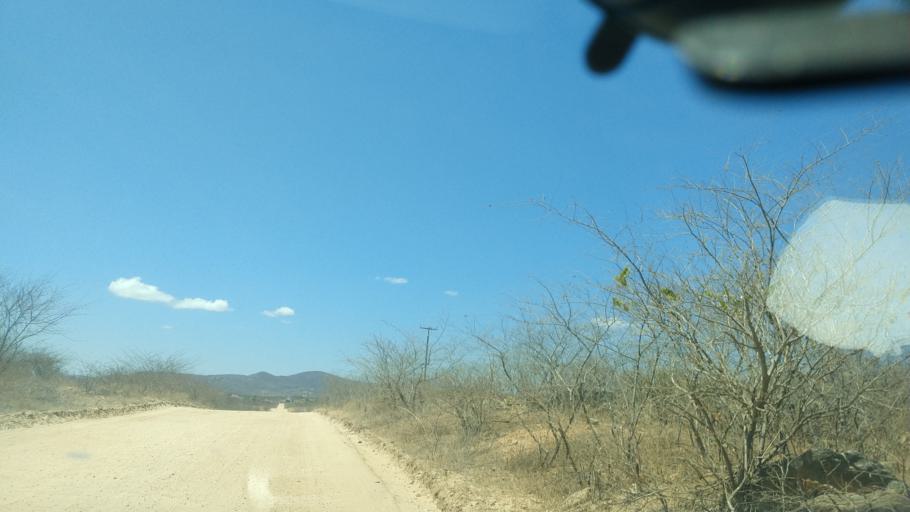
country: BR
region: Rio Grande do Norte
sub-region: Sao Tome
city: Sao Tome
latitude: -5.9735
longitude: -36.1663
